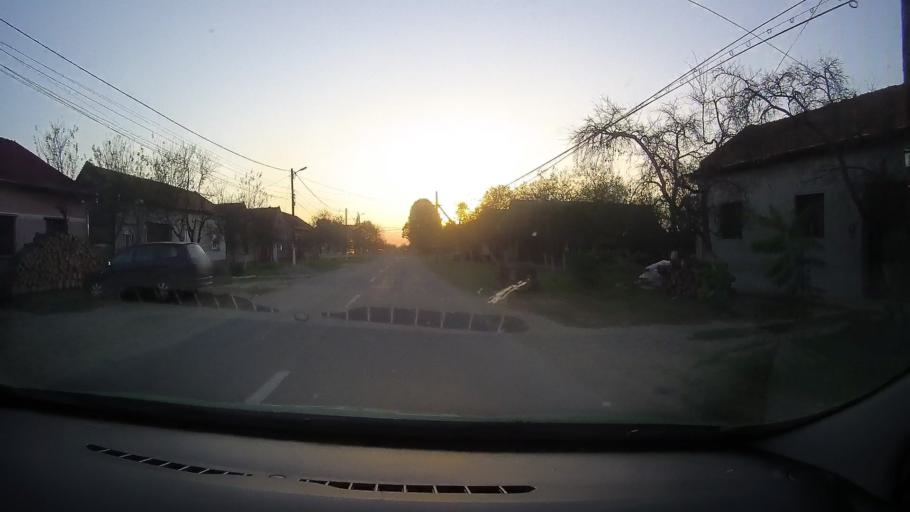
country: RO
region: Timis
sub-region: Comuna Manastiur
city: Manastiur
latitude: 45.8329
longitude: 22.0668
